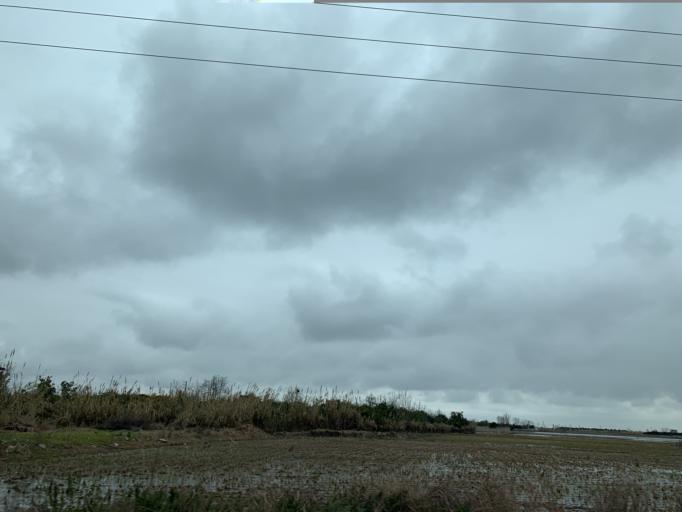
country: IR
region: Mazandaran
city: Babol
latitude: 36.5204
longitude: 52.5938
